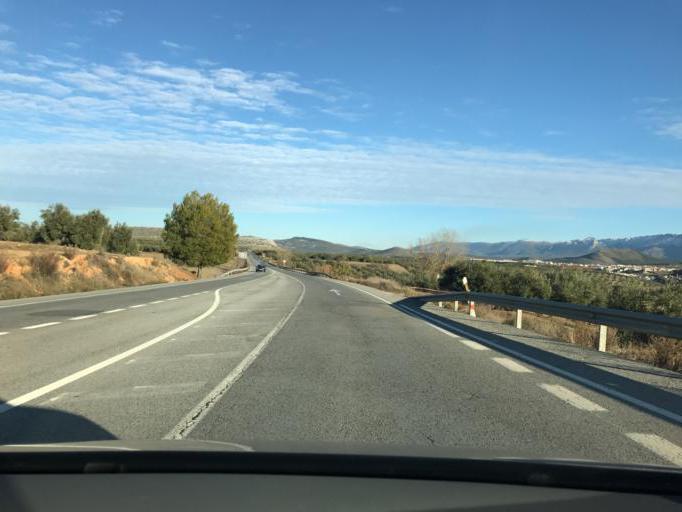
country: ES
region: Andalusia
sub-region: Provincia de Granada
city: Iznalloz
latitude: 37.3996
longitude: -3.5495
